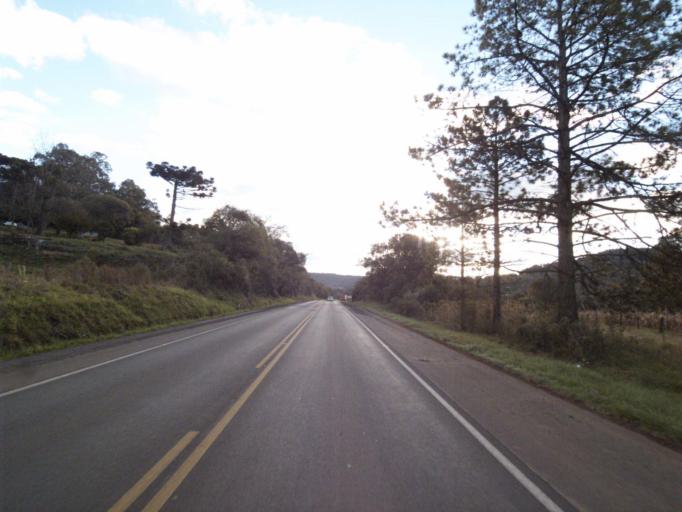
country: BR
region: Santa Catarina
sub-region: Joacaba
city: Joacaba
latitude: -27.2873
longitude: -51.4268
